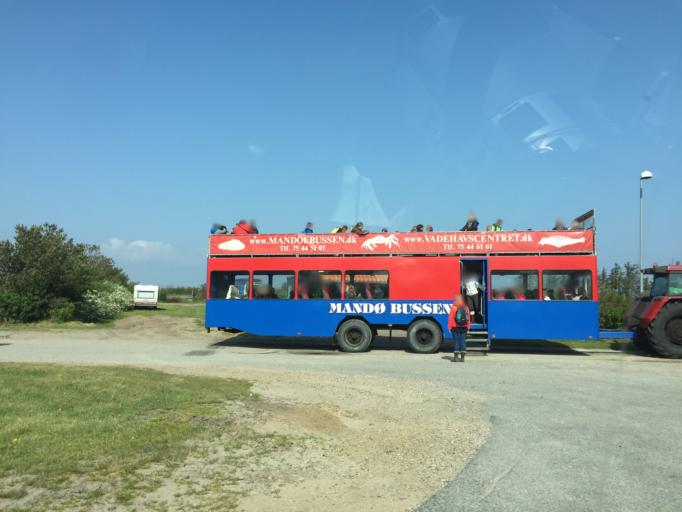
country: DK
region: South Denmark
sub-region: Esbjerg Kommune
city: Ribe
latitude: 55.2963
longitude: 8.6703
